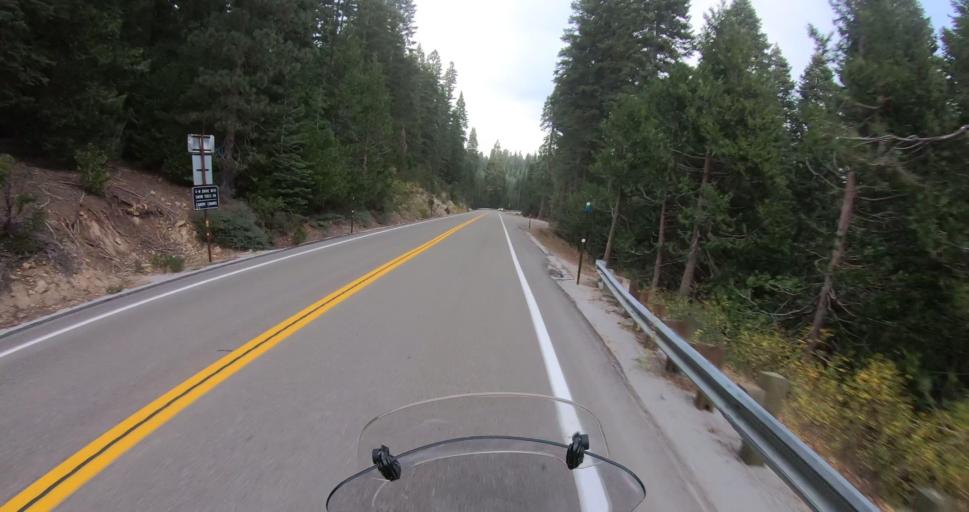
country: US
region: California
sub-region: Calaveras County
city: Arnold
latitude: 38.3903
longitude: -120.1829
